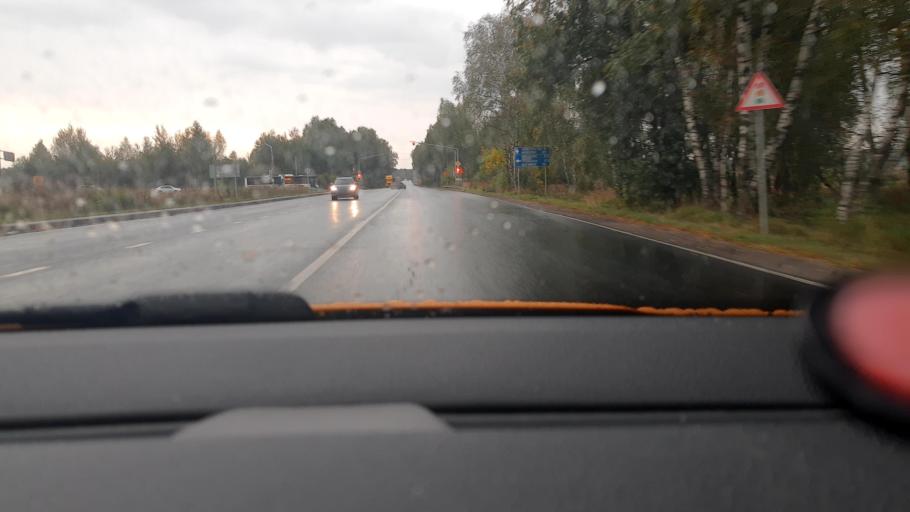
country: RU
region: Moskovskaya
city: Obukhovo
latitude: 55.8005
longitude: 38.2507
